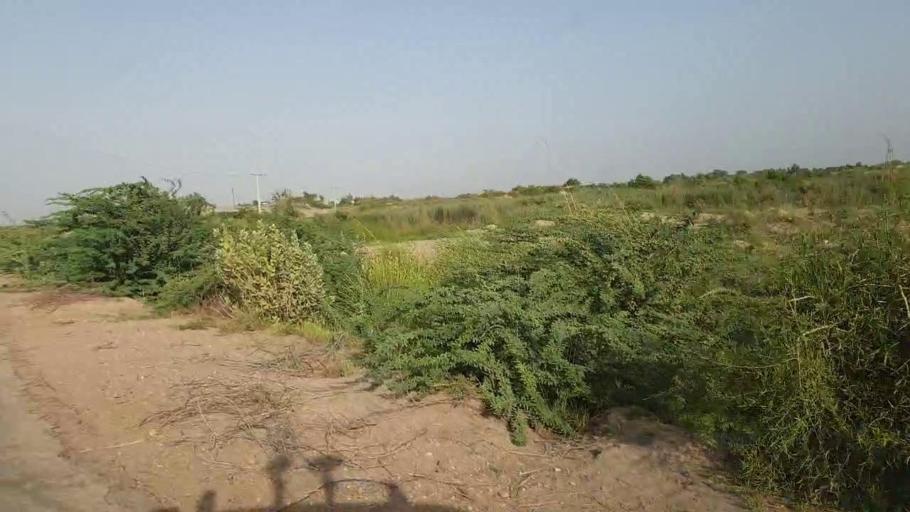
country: PK
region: Sindh
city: Jam Sahib
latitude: 26.4387
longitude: 68.8656
